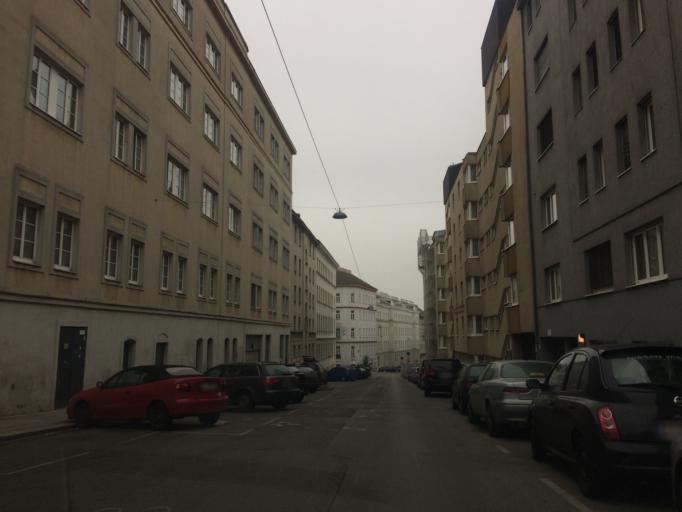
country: AT
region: Vienna
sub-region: Wien Stadt
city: Vienna
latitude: 48.1974
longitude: 16.3162
